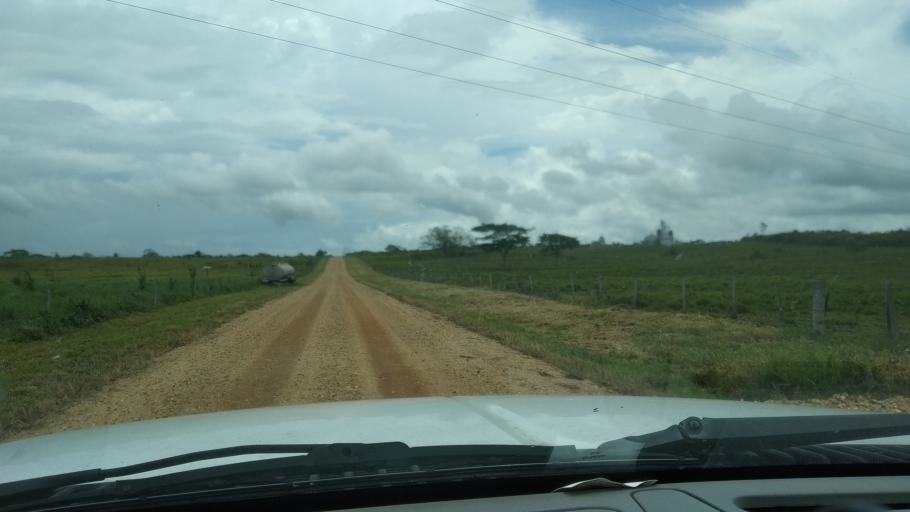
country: BZ
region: Cayo
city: San Ignacio
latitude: 17.2314
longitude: -88.9723
